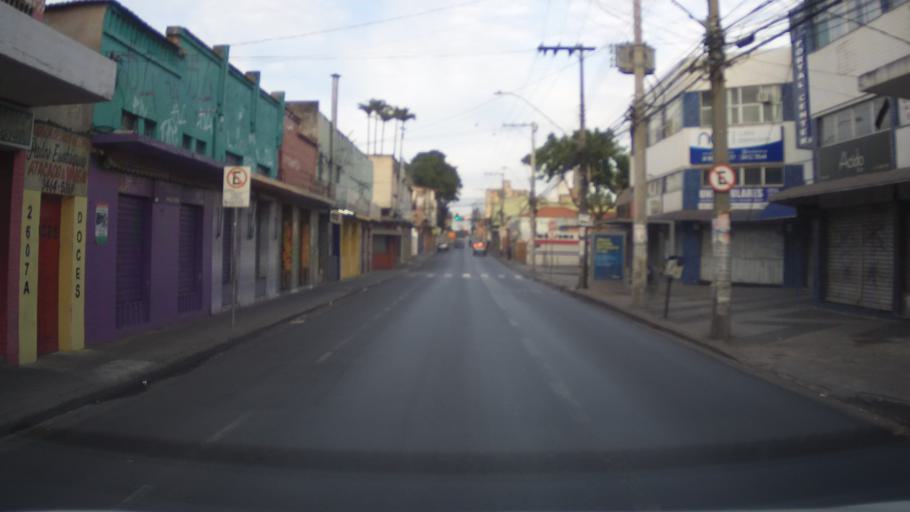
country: BR
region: Minas Gerais
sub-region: Belo Horizonte
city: Belo Horizonte
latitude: -19.9150
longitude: -43.9771
